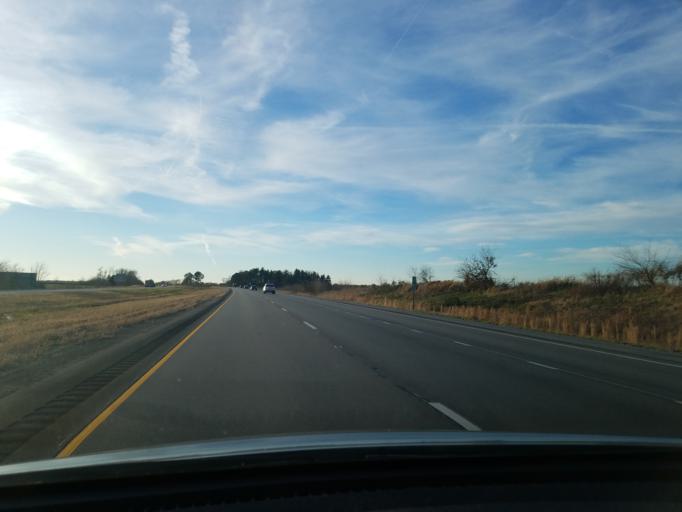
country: US
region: Indiana
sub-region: Spencer County
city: Dale
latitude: 38.1957
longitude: -86.9906
